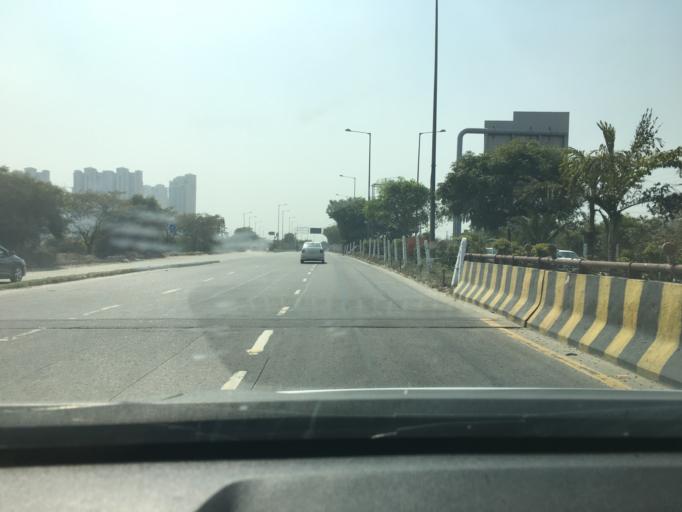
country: IN
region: Uttar Pradesh
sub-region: Gautam Buddha Nagar
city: Greater Noida
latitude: 28.4475
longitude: 77.4890
